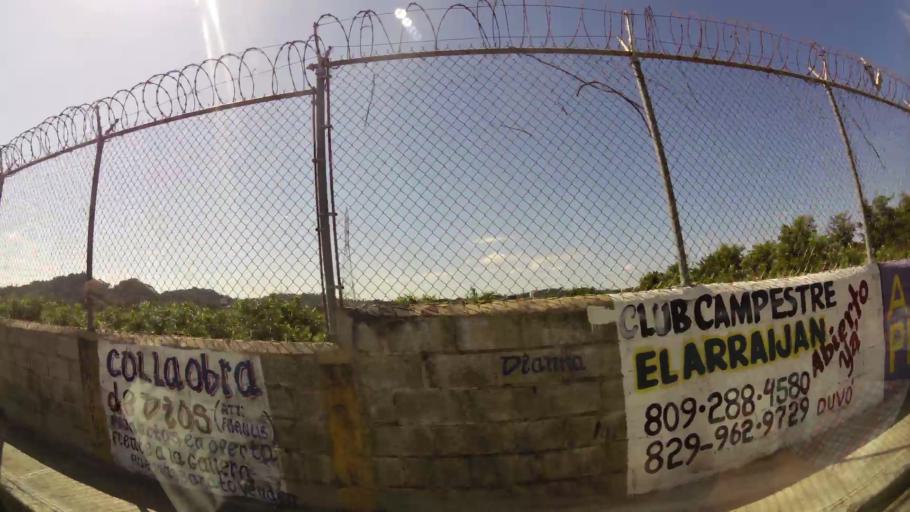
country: DO
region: San Cristobal
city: San Cristobal
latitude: 18.4257
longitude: -70.1315
